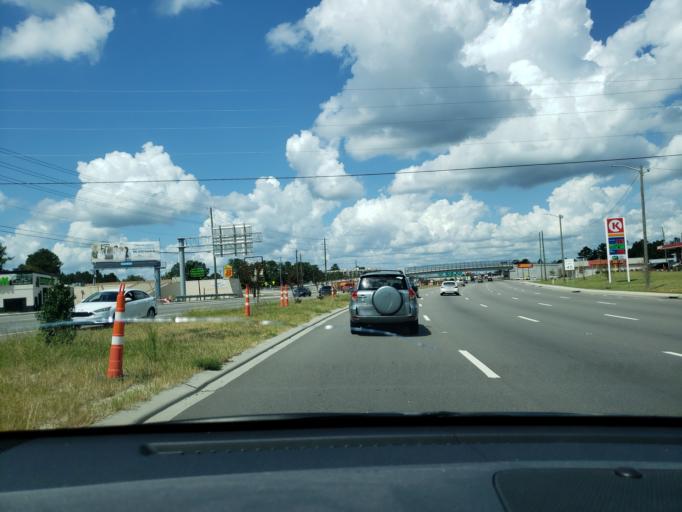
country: US
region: North Carolina
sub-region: Cumberland County
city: Spring Lake
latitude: 35.1612
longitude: -78.9719
